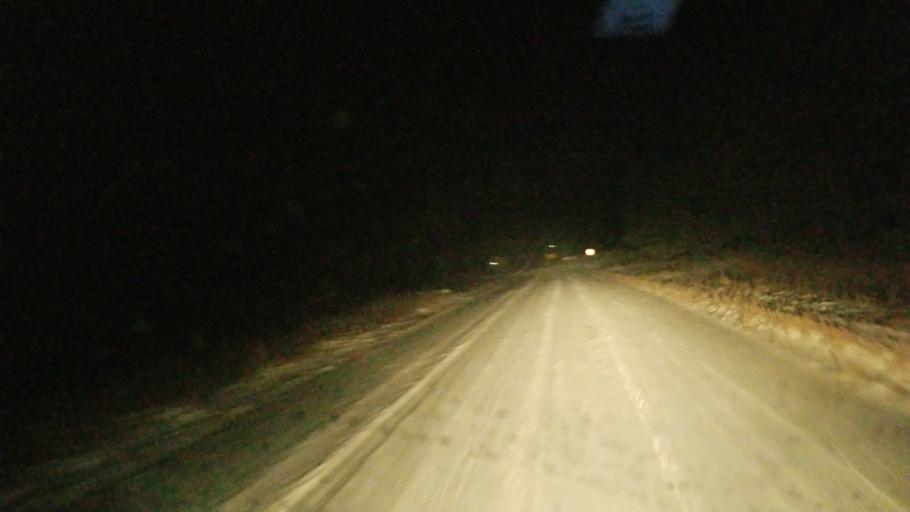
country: US
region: Michigan
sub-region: Osceola County
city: Reed City
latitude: 43.8425
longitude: -85.4141
